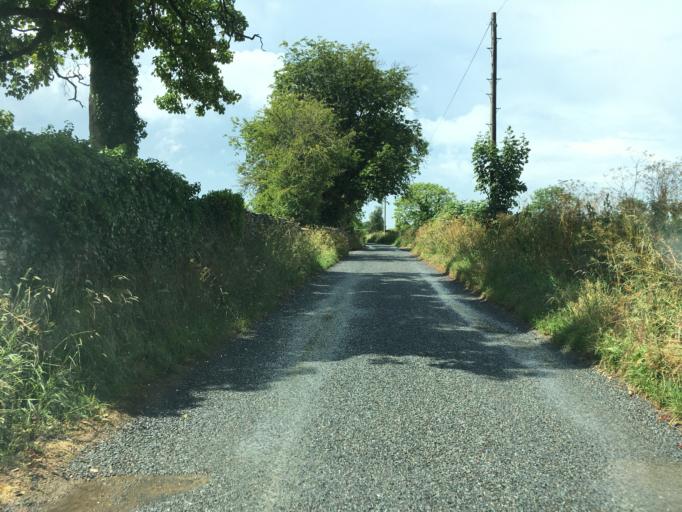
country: GB
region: England
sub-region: Wiltshire
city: Luckington
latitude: 51.6177
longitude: -2.2520
